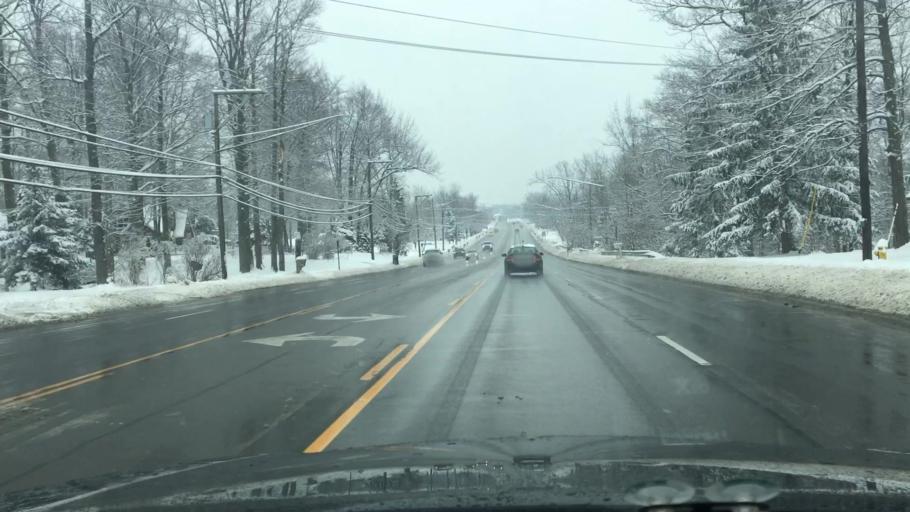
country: US
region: New York
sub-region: Erie County
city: Orchard Park
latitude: 42.8084
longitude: -78.7519
